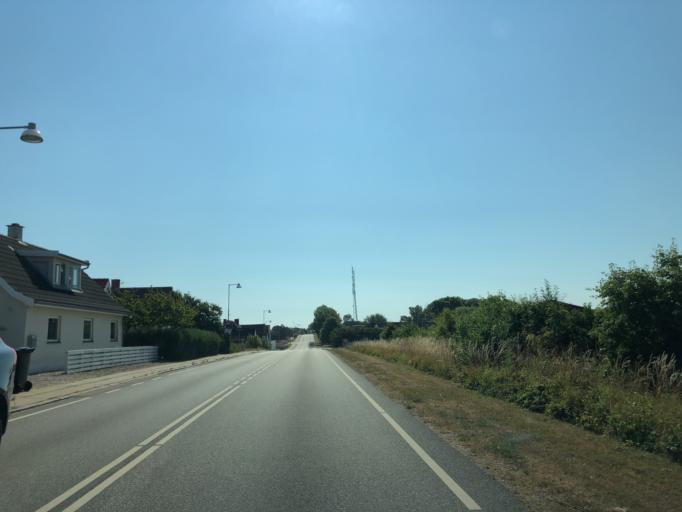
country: DK
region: Zealand
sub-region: Odsherred Kommune
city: Asnaes
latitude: 55.9721
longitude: 11.3556
